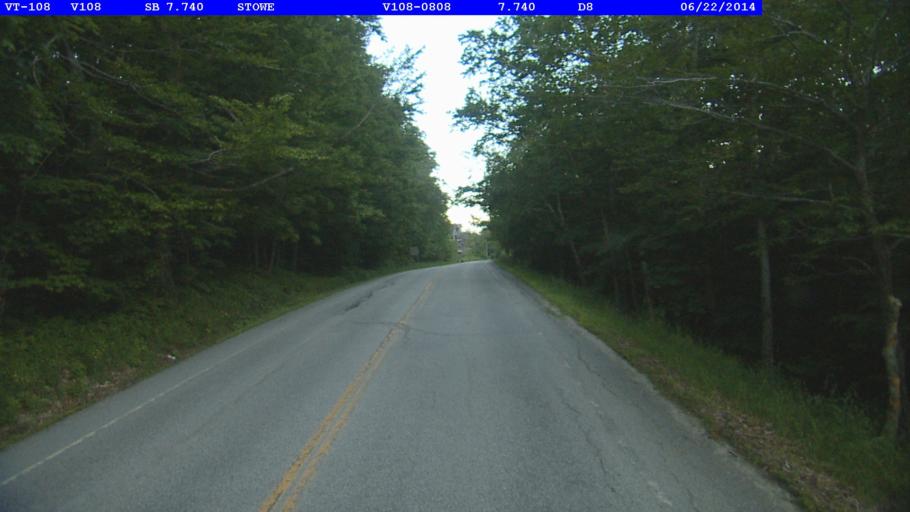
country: US
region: Vermont
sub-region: Lamoille County
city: Johnson
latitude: 44.5321
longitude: -72.7851
